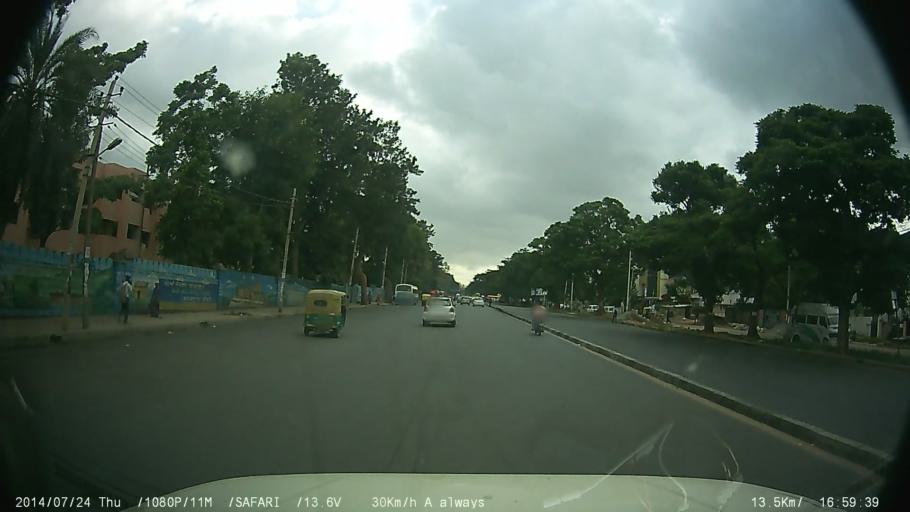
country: IN
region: Karnataka
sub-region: Bangalore Urban
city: Bangalore
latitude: 12.9251
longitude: 77.6361
